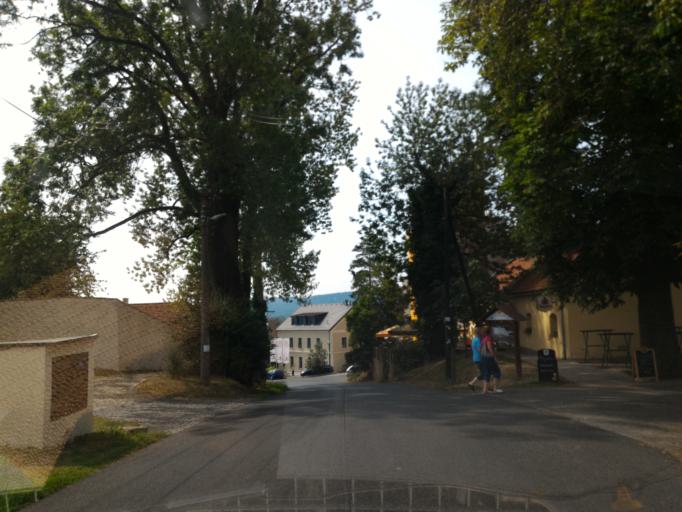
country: CZ
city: Prisovice
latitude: 50.5735
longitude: 15.0544
